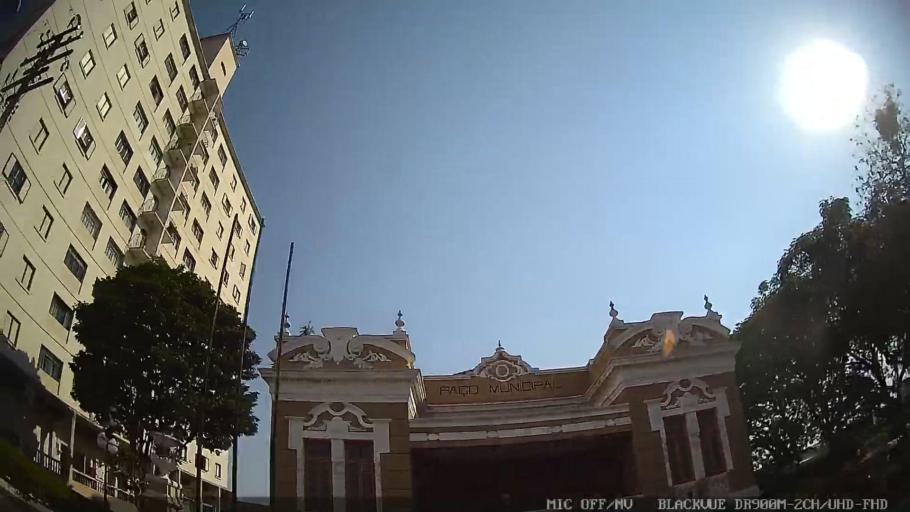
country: BR
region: Sao Paulo
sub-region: Itatiba
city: Itatiba
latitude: -23.0054
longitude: -46.8412
